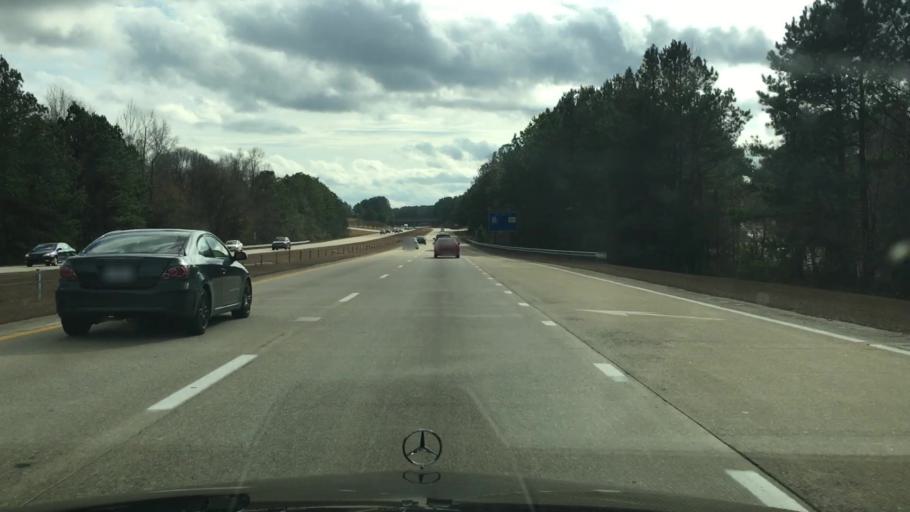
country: US
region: North Carolina
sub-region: Johnston County
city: Benson
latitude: 35.4301
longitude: -78.5322
